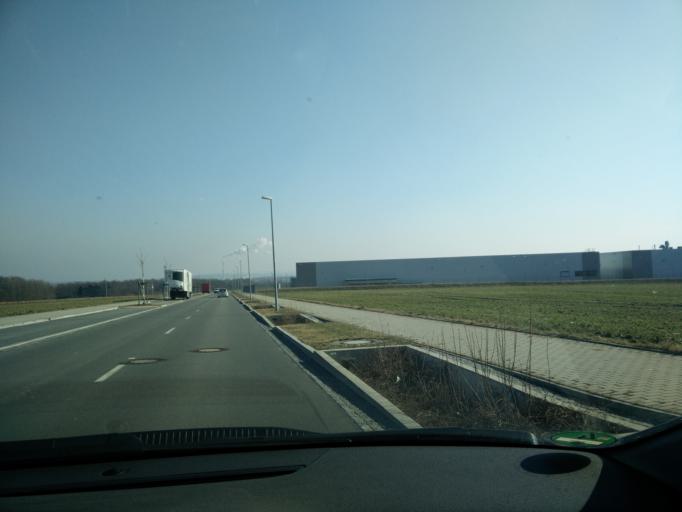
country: DE
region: Saxony
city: Wittgensdorf
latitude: 50.8745
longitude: 12.8351
